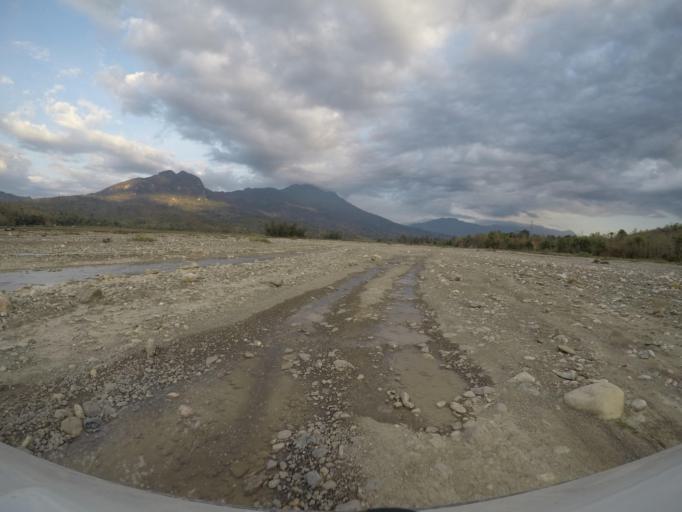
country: TL
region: Bobonaro
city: Maliana
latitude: -8.9059
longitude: 125.2106
